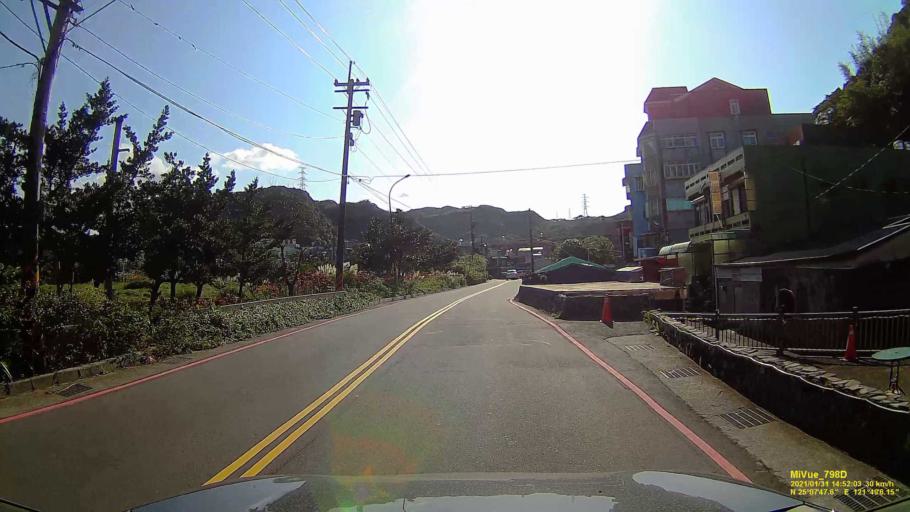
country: TW
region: Taiwan
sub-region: Keelung
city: Keelung
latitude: 25.1296
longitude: 121.8180
